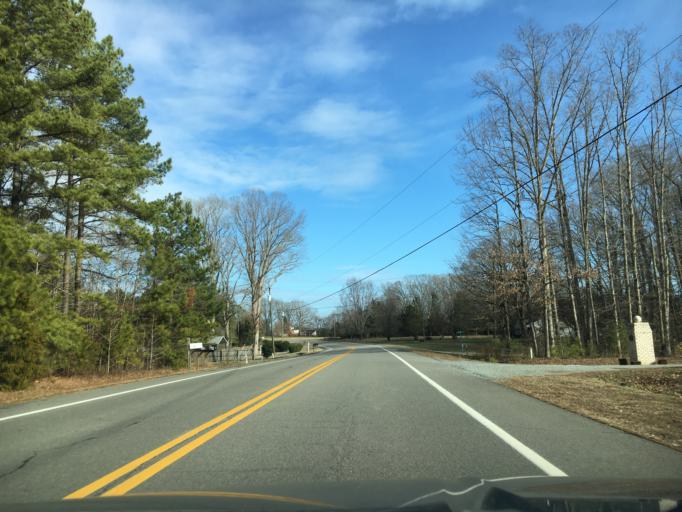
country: US
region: Virginia
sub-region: Halifax County
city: South Boston
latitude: 36.7351
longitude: -78.8544
